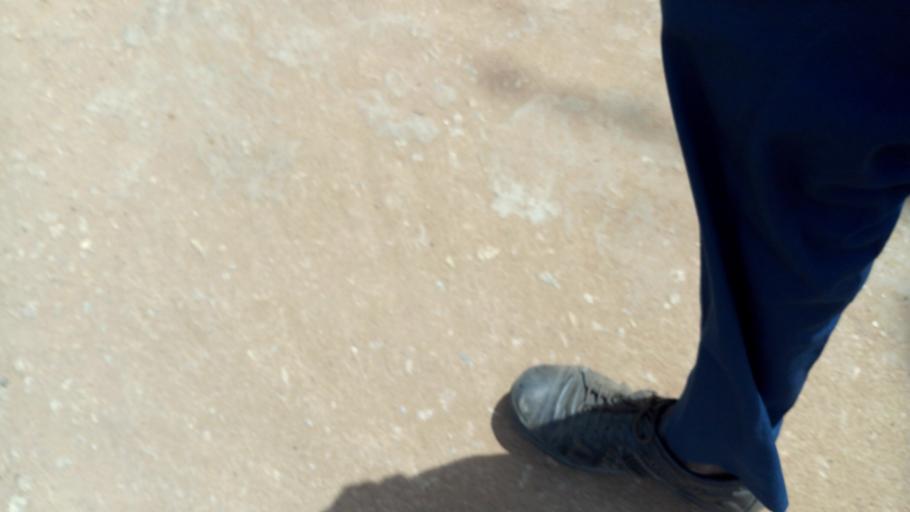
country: CI
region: Vallee du Bandama
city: Bouake
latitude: 7.7165
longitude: -5.0341
